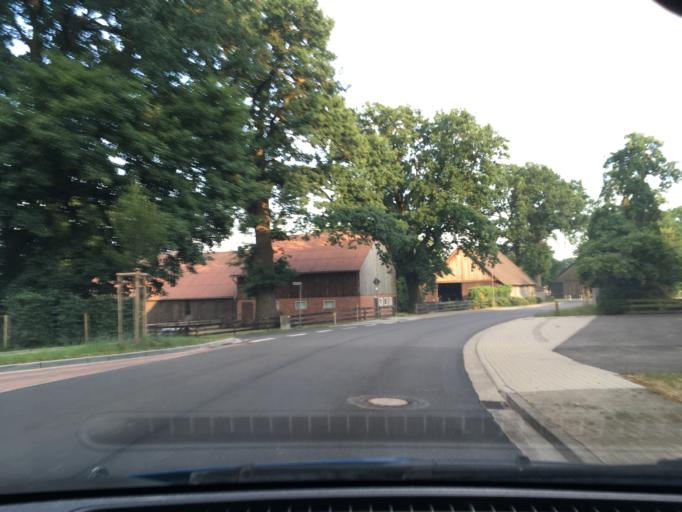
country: DE
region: Lower Saxony
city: Scharnhorst
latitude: 52.7184
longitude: 10.3135
